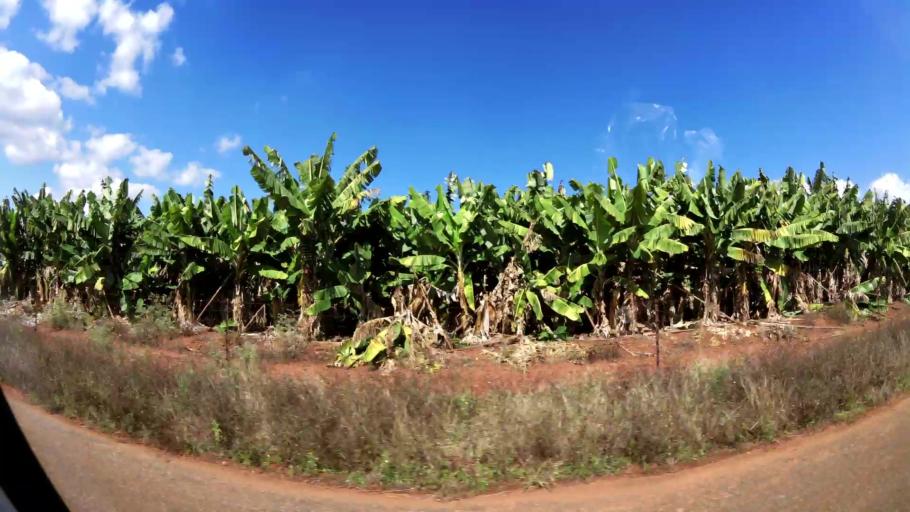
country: ZA
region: Limpopo
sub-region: Mopani District Municipality
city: Tzaneen
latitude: -23.7980
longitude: 30.1362
